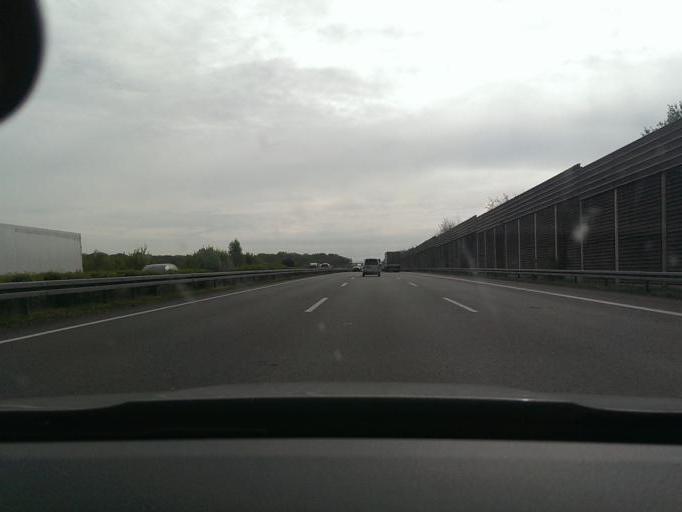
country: DE
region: Lower Saxony
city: Lehre
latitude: 52.3094
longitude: 10.6617
